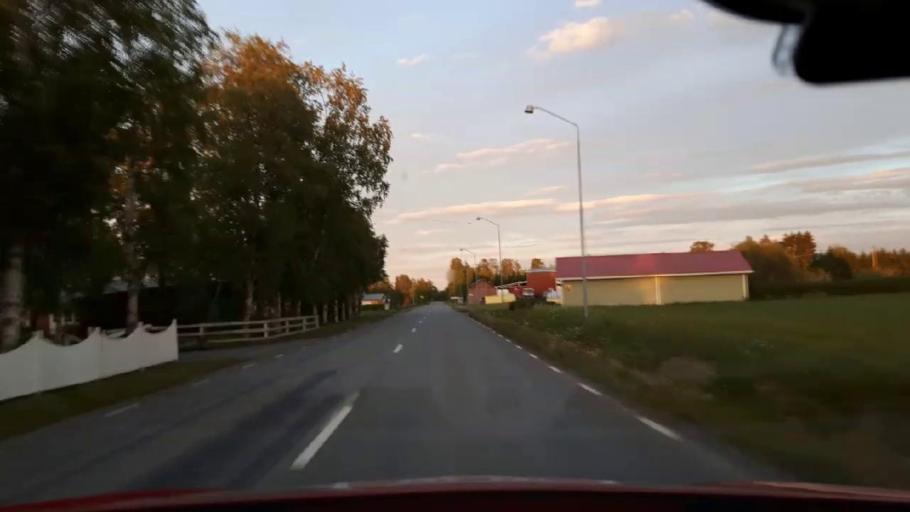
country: SE
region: Jaemtland
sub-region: OEstersunds Kommun
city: Ostersund
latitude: 63.1178
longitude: 14.7206
